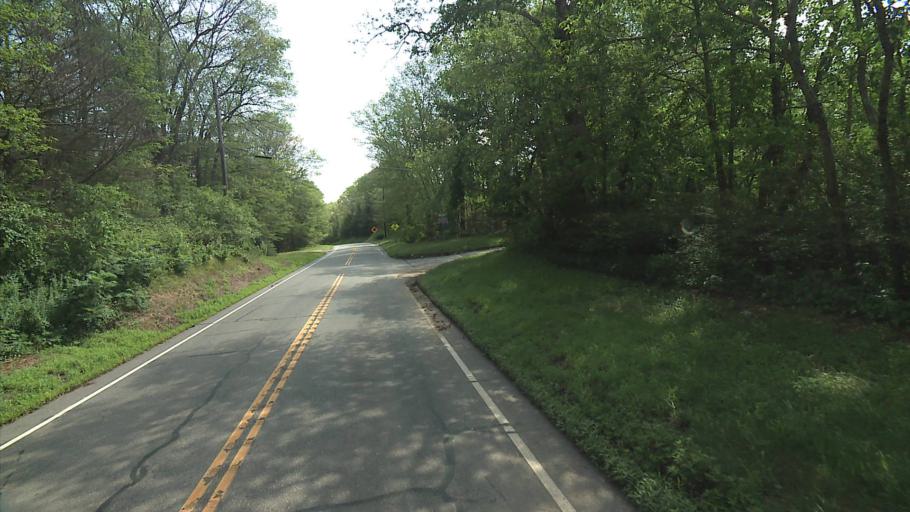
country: US
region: Connecticut
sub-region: New London County
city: Baltic
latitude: 41.7002
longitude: -72.0587
